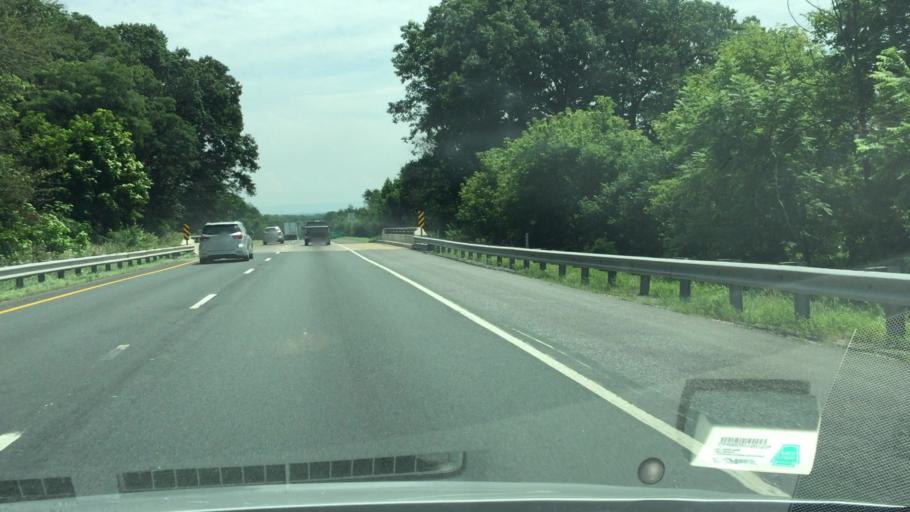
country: US
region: Maryland
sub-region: Washington County
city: Wilson-Conococheague
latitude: 39.6520
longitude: -77.9096
